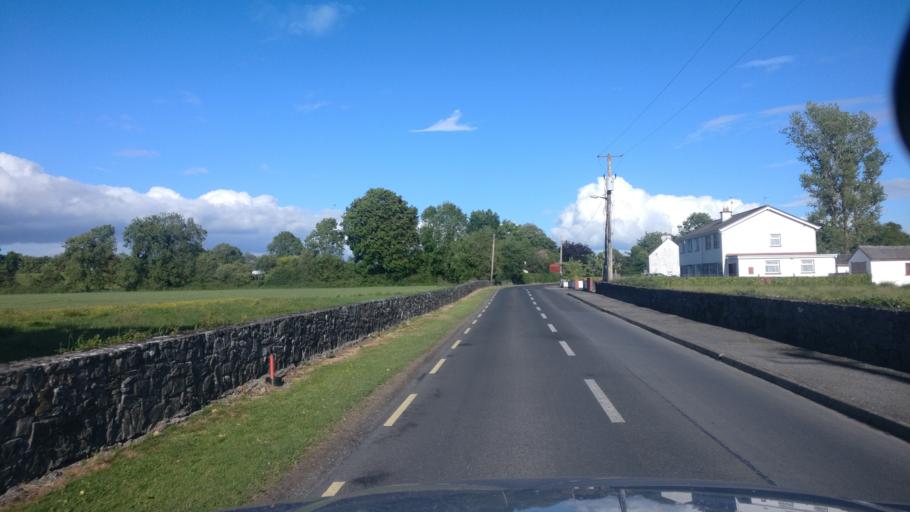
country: IE
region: Connaught
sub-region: County Galway
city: Ballinasloe
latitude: 53.2353
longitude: -8.2685
